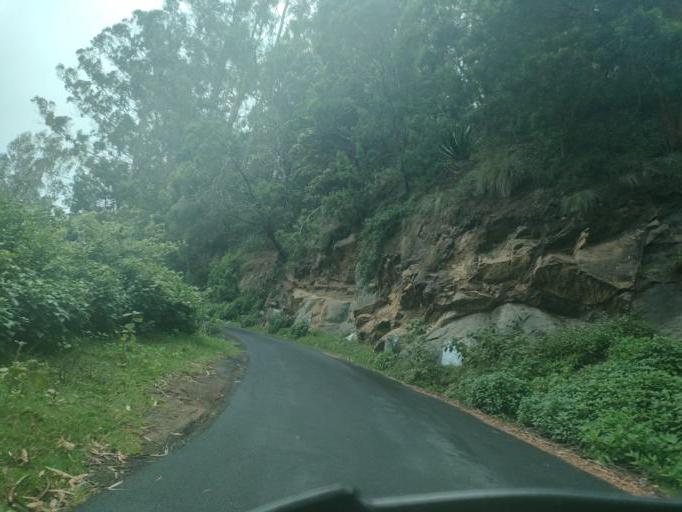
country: IN
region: Tamil Nadu
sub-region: Dindigul
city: Kodaikanal
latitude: 10.2428
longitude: 77.3614
